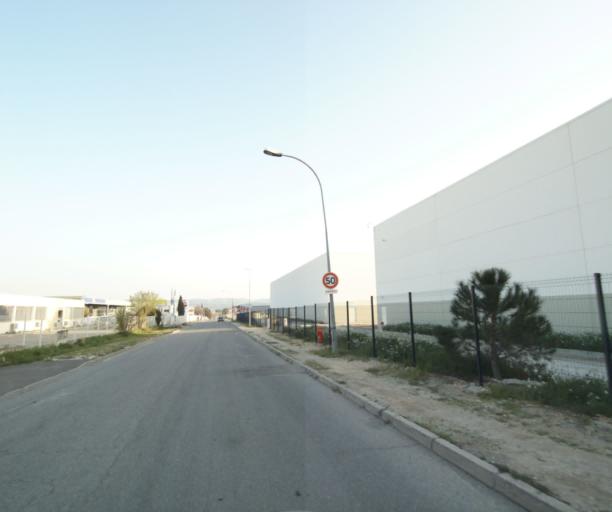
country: FR
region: Provence-Alpes-Cote d'Azur
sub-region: Departement des Bouches-du-Rhone
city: Saint-Victoret
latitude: 43.4348
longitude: 5.2522
